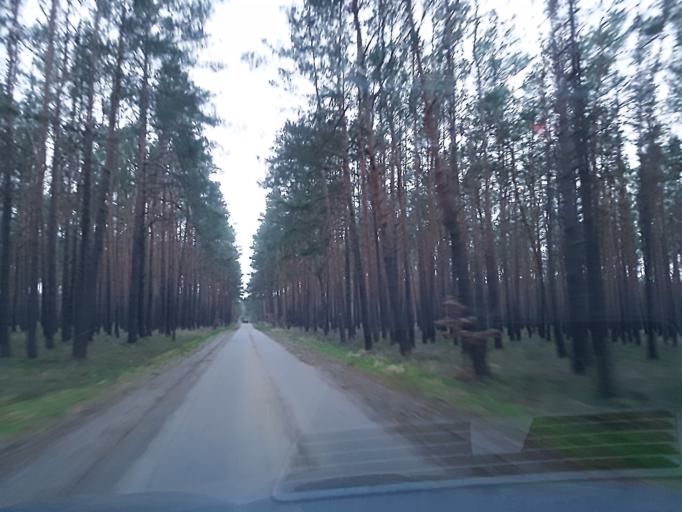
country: DE
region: Brandenburg
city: Schonewalde
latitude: 51.6536
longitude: 13.6255
